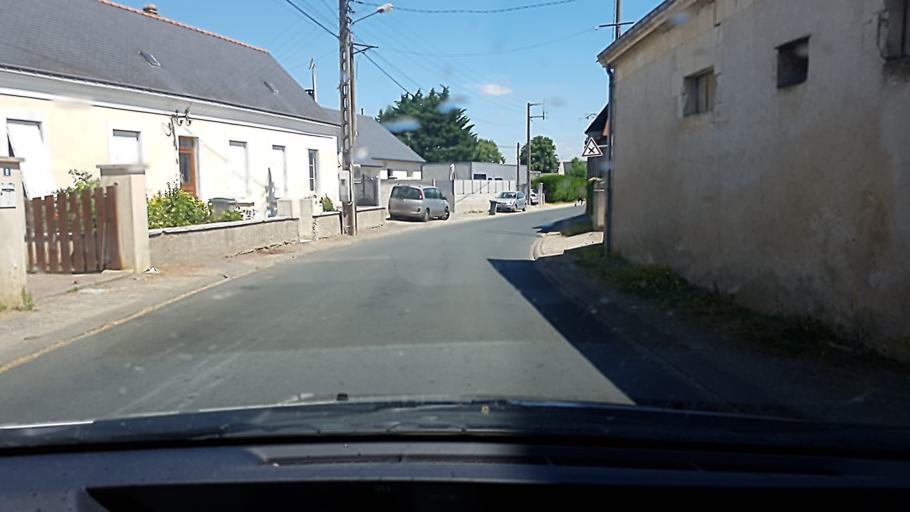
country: FR
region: Pays de la Loire
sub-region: Departement de Maine-et-Loire
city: Corze
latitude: 47.5278
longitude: -0.4015
